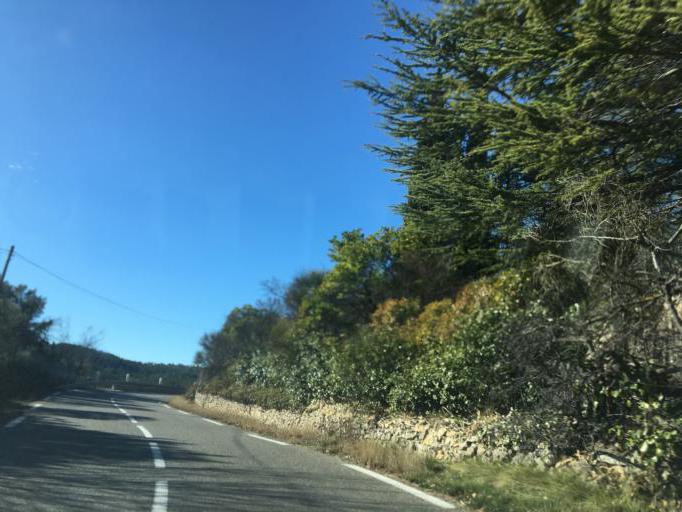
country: FR
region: Provence-Alpes-Cote d'Azur
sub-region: Departement du Var
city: Barjols
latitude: 43.5997
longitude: 5.9558
